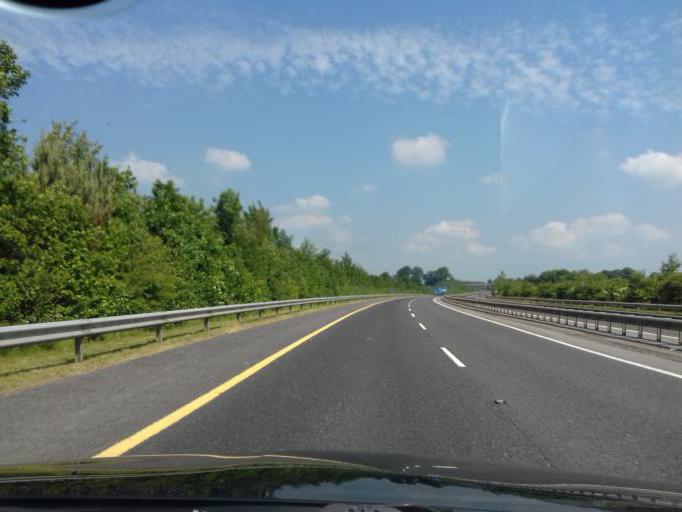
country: IE
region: Leinster
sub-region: An Mhi
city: Ashbourne
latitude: 53.5113
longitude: -6.4210
